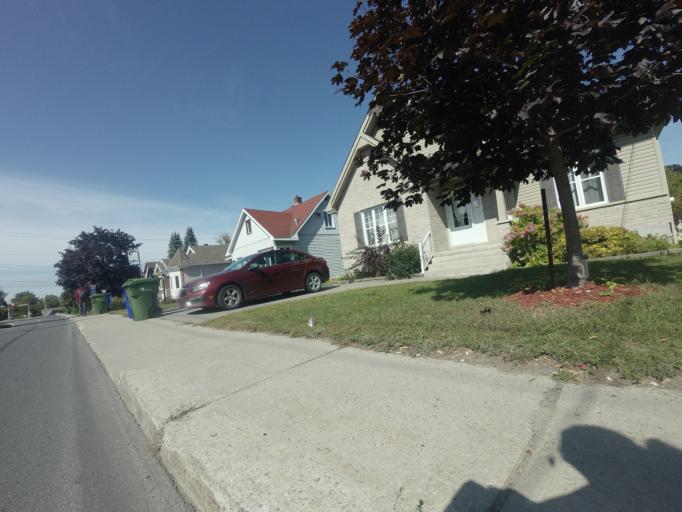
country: CA
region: Quebec
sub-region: Laurentides
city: Saint-Eustache
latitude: 45.5618
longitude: -73.9142
